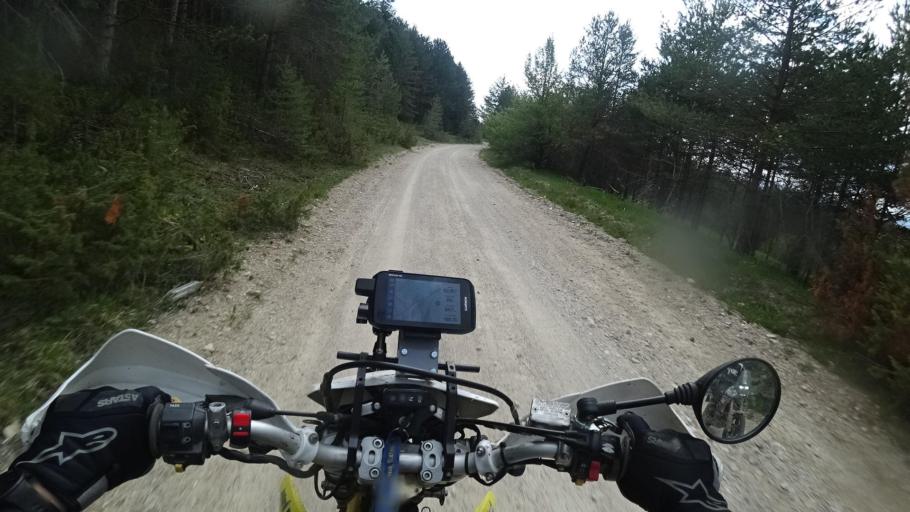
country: BA
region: Federation of Bosnia and Herzegovina
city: Glamoc
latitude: 44.0883
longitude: 16.8650
